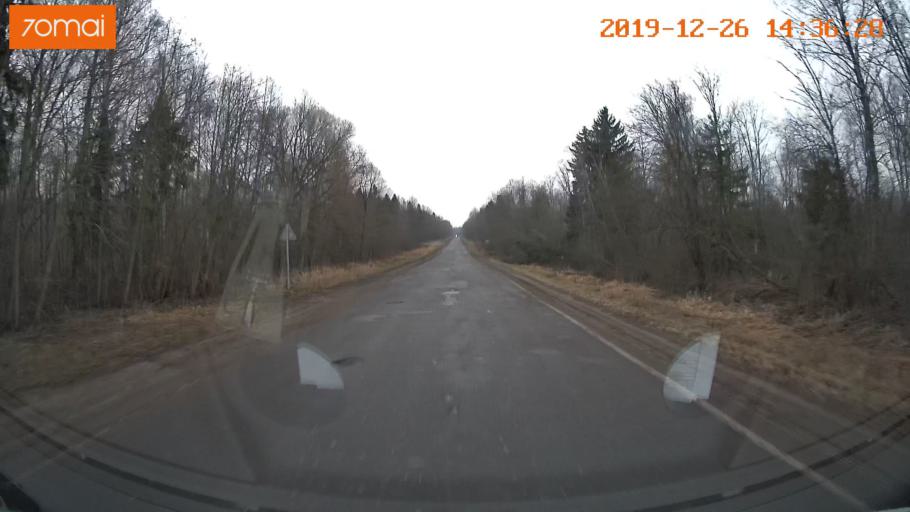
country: RU
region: Jaroslavl
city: Poshekhon'ye
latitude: 58.4110
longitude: 38.9759
